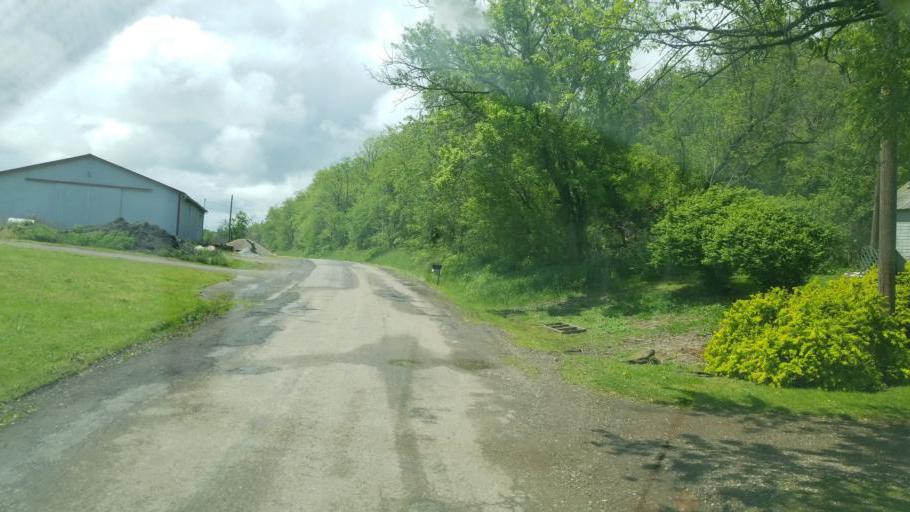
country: US
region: Ohio
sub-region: Tuscarawas County
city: Dennison
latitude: 40.3785
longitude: -81.2466
